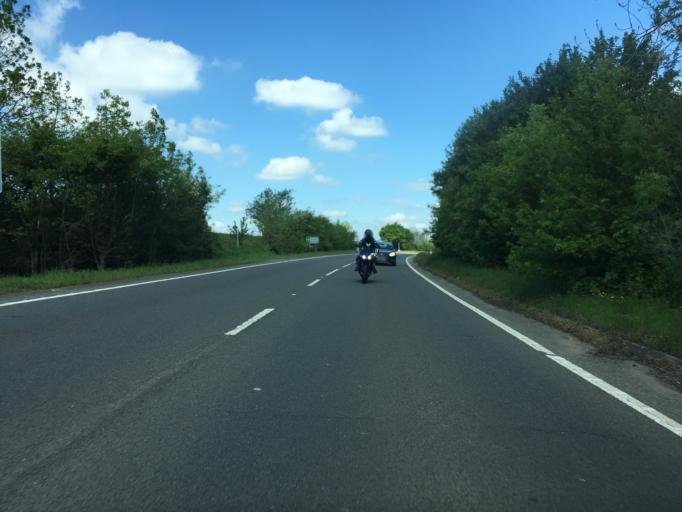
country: GB
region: England
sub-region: Northamptonshire
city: Brackley
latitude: 52.0237
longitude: -1.1560
